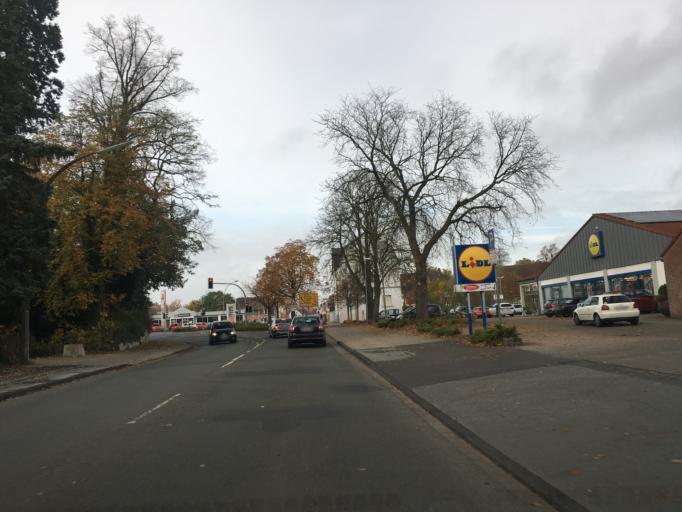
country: DE
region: North Rhine-Westphalia
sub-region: Regierungsbezirk Munster
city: Steinfurt
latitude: 52.1178
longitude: 7.3964
